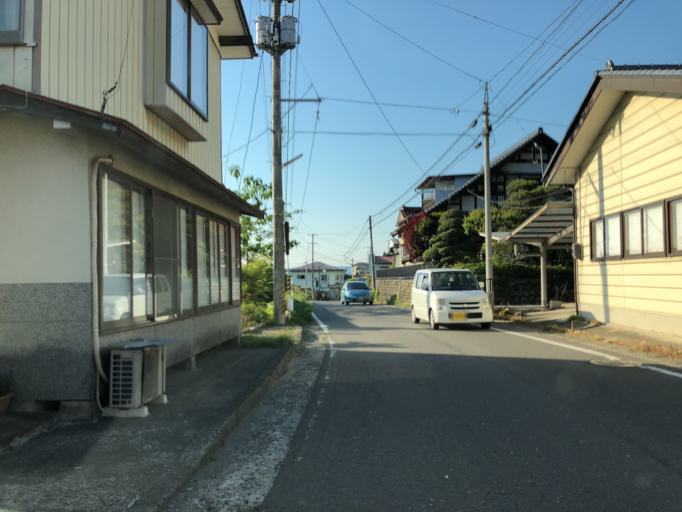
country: JP
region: Ibaraki
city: Daigo
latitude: 36.9334
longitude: 140.4462
